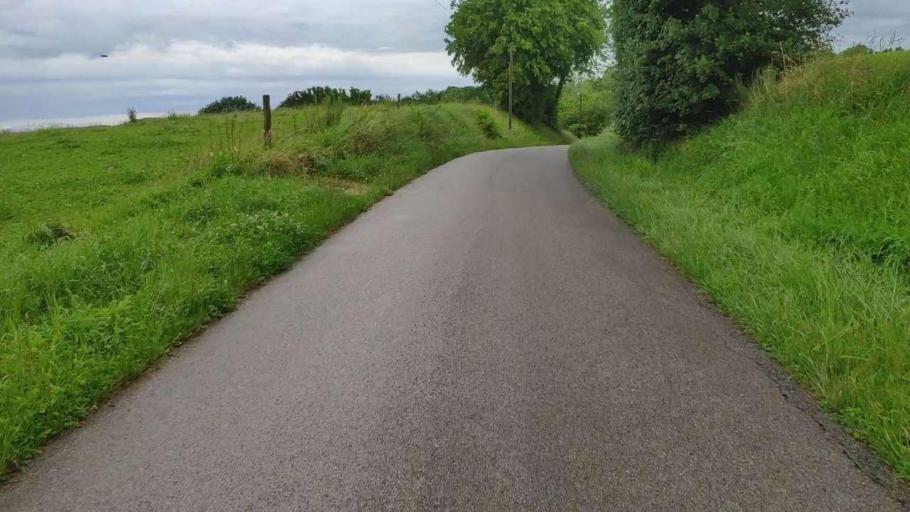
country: FR
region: Franche-Comte
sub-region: Departement du Jura
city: Poligny
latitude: 46.7861
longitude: 5.6073
